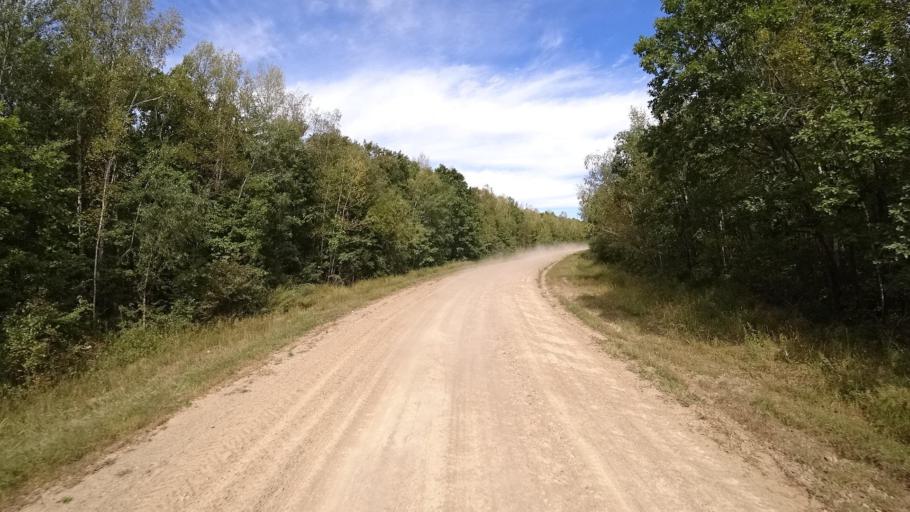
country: RU
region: Primorskiy
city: Yakovlevka
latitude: 44.6588
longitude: 133.5967
